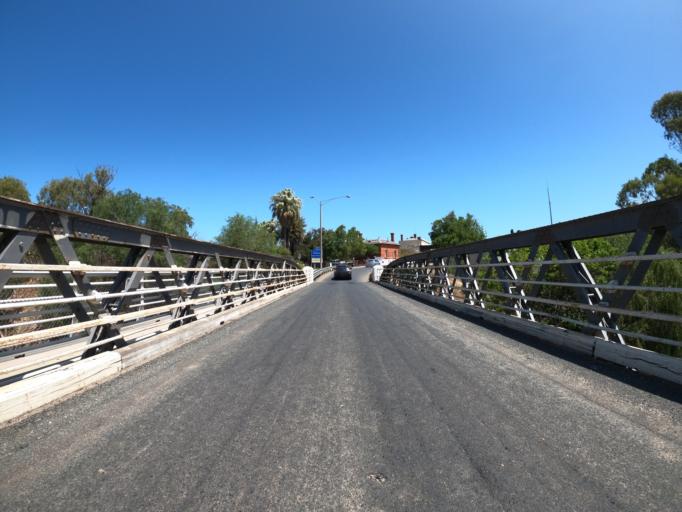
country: AU
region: New South Wales
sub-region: Corowa Shire
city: Corowa
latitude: -36.0071
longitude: 146.3952
